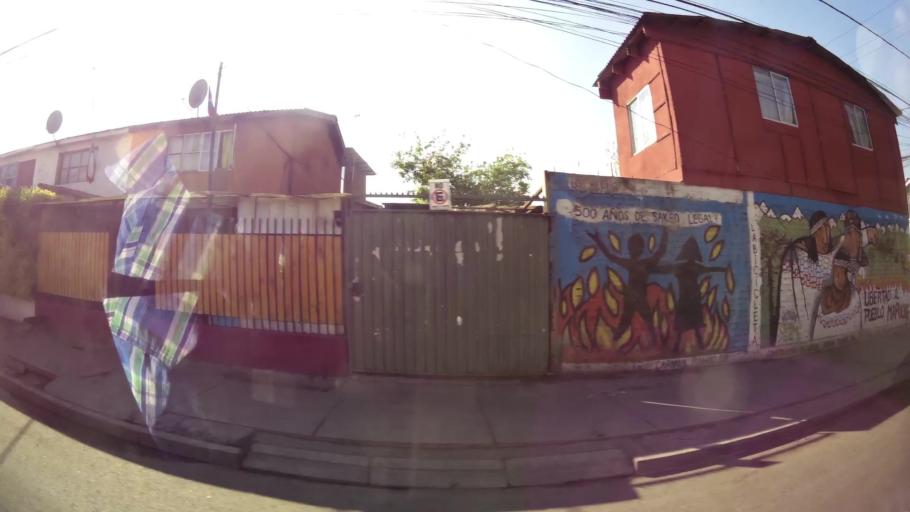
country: CL
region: Santiago Metropolitan
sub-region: Provincia de Santiago
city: Lo Prado
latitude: -33.4610
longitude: -70.7567
